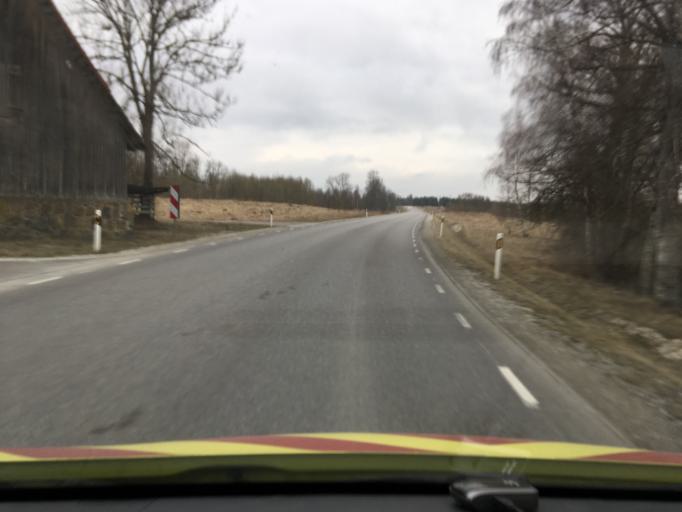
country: EE
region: Raplamaa
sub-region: Rapla vald
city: Rapla
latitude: 58.9997
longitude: 24.8426
